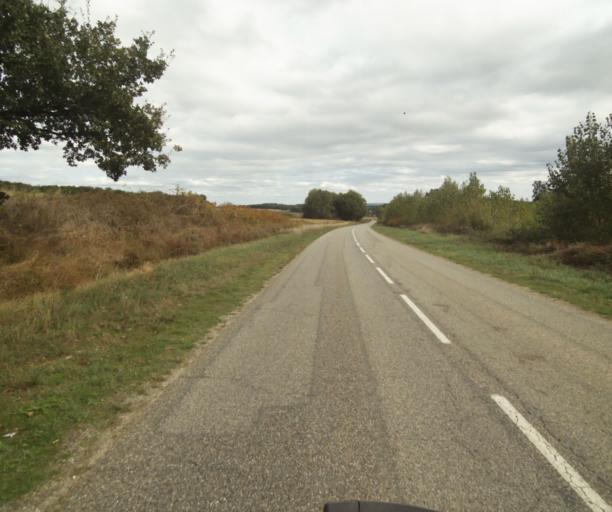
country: FR
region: Midi-Pyrenees
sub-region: Departement du Tarn-et-Garonne
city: Verdun-sur-Garonne
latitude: 43.8583
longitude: 1.1174
